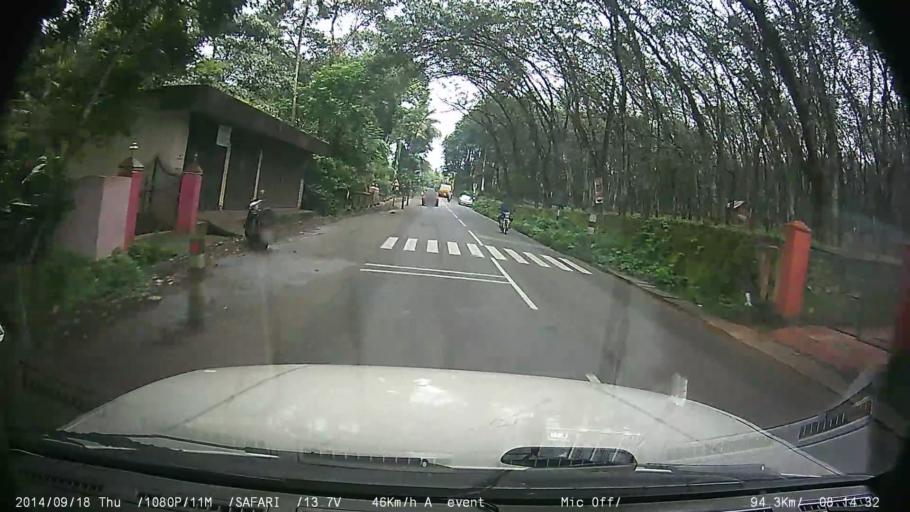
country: IN
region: Kerala
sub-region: Kottayam
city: Kottayam
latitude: 9.6237
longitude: 76.6036
